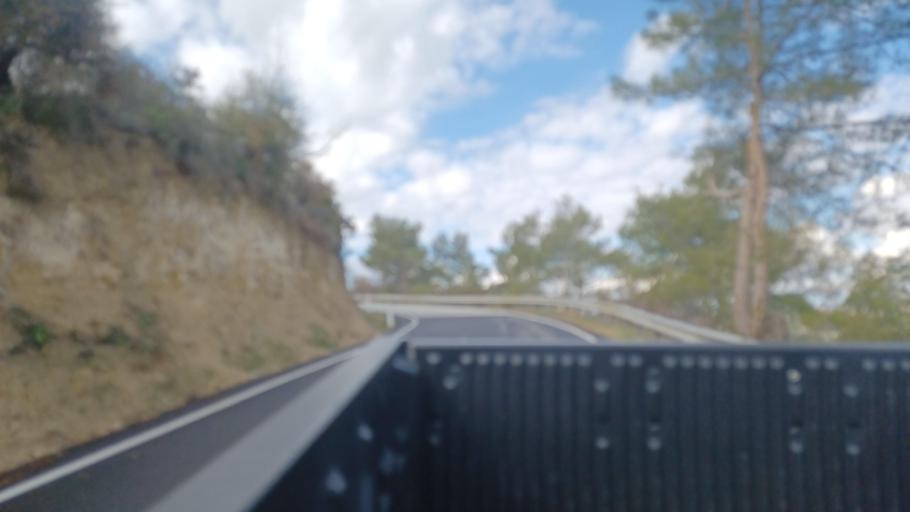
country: CY
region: Limassol
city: Pissouri
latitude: 34.7469
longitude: 32.6615
